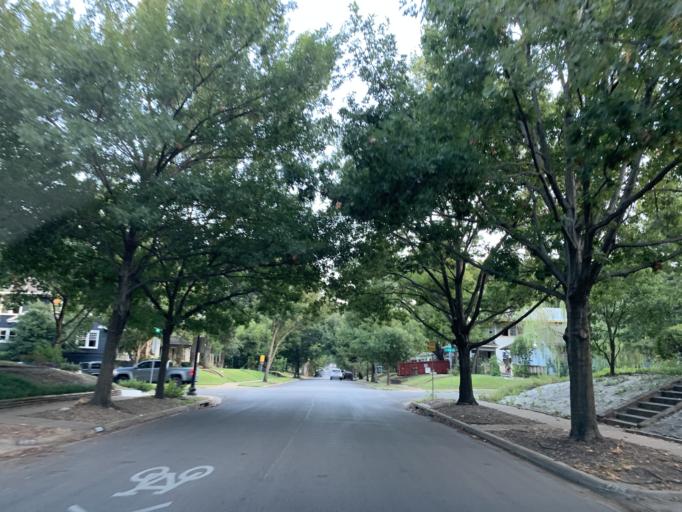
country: US
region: Texas
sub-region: Dallas County
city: Cockrell Hill
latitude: 32.7468
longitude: -96.8441
